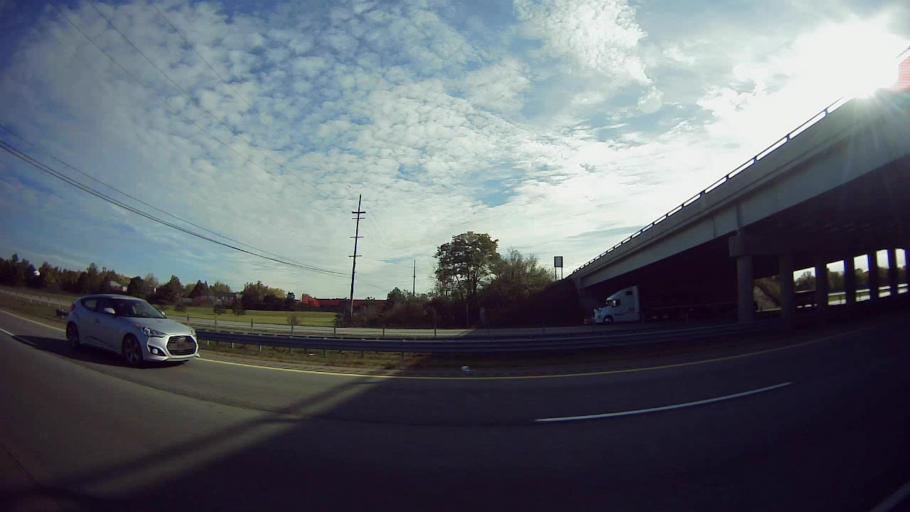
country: US
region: Michigan
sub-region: Wayne County
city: Plymouth
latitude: 42.3597
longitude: -83.4362
